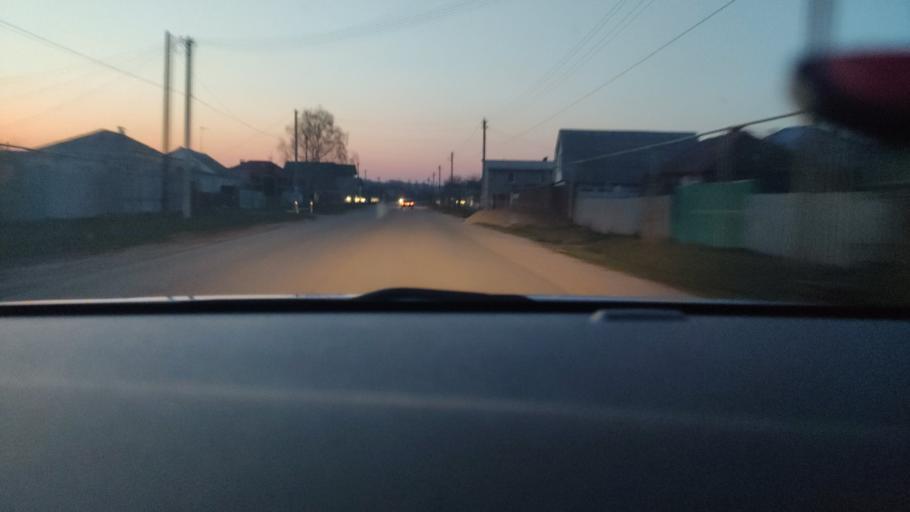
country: RU
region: Voronezj
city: Shilovo
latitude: 51.4858
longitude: 39.0157
